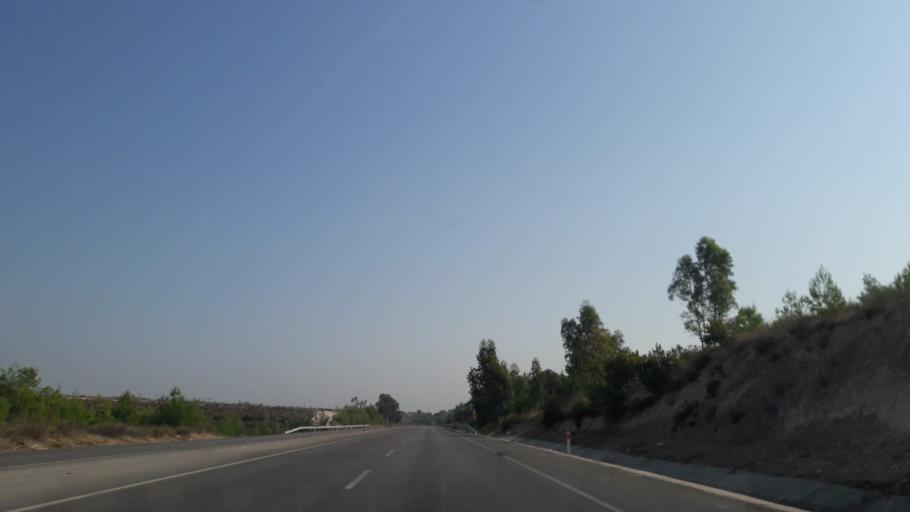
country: TR
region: Adana
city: Sagkaya
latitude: 37.1550
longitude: 35.5484
